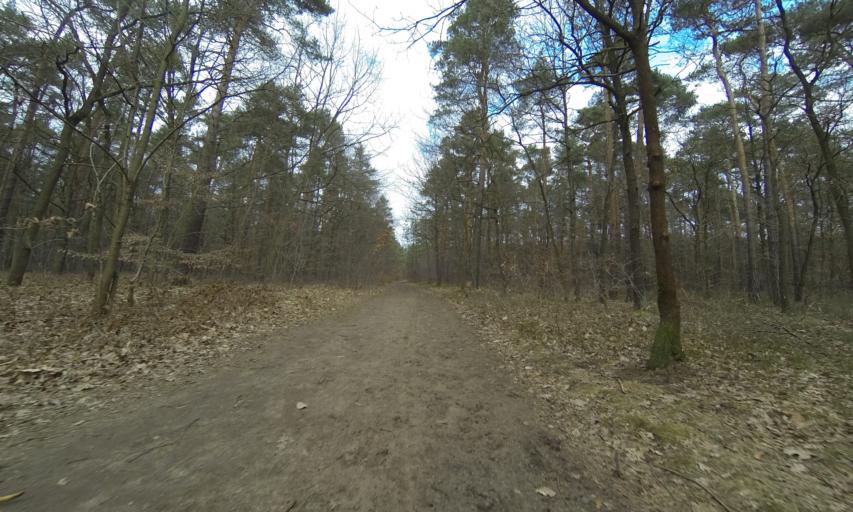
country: DE
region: Saxony
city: Radebeul
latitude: 51.1034
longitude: 13.6985
